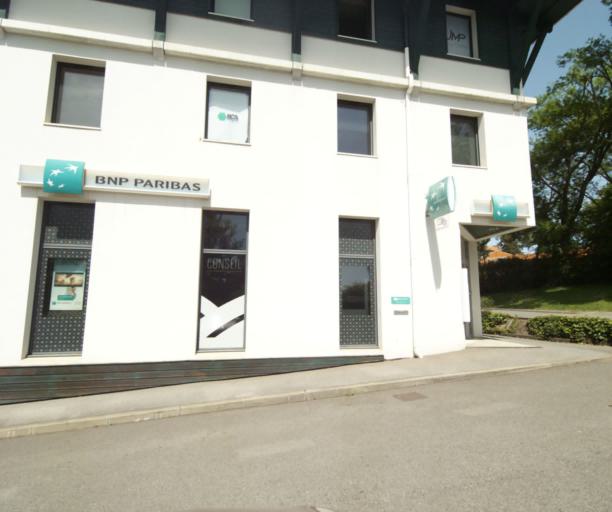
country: FR
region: Aquitaine
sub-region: Departement des Pyrenees-Atlantiques
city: Mouguerre
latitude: 43.4705
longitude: -1.4468
